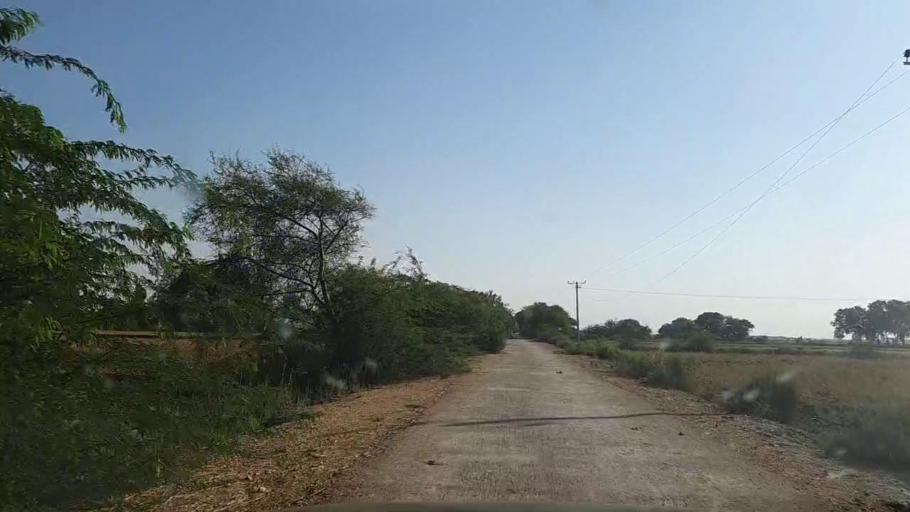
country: PK
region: Sindh
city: Daro Mehar
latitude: 24.6467
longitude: 68.0751
